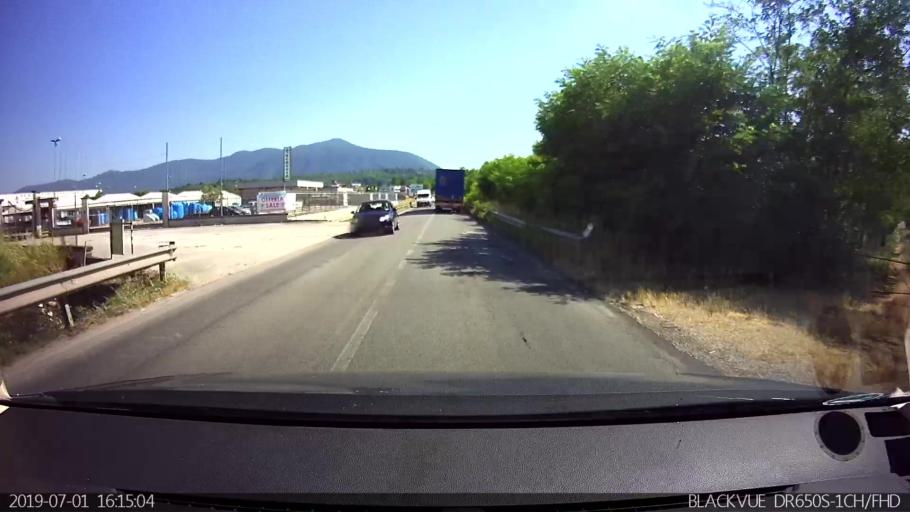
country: IT
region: Latium
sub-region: Provincia di Frosinone
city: Ceccano
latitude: 41.5963
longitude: 13.2921
